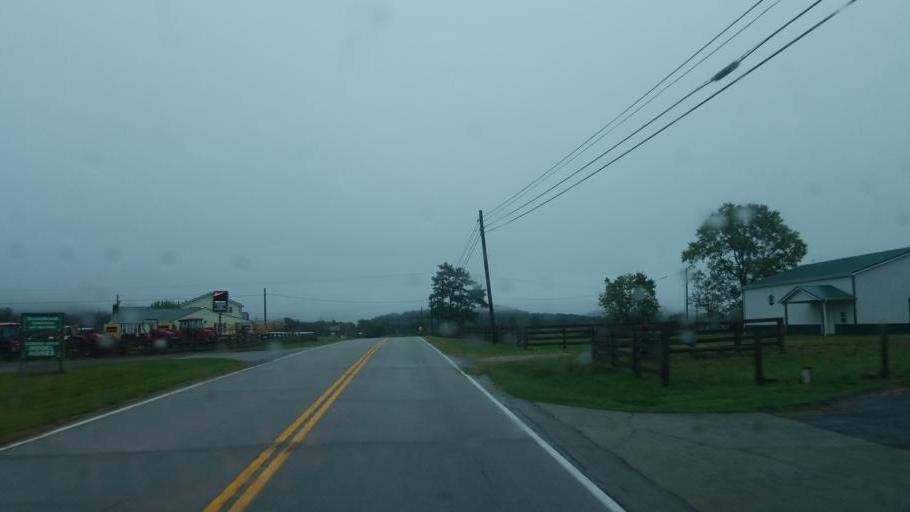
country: US
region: Kentucky
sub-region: Fleming County
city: Flemingsburg
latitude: 38.3869
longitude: -83.6651
